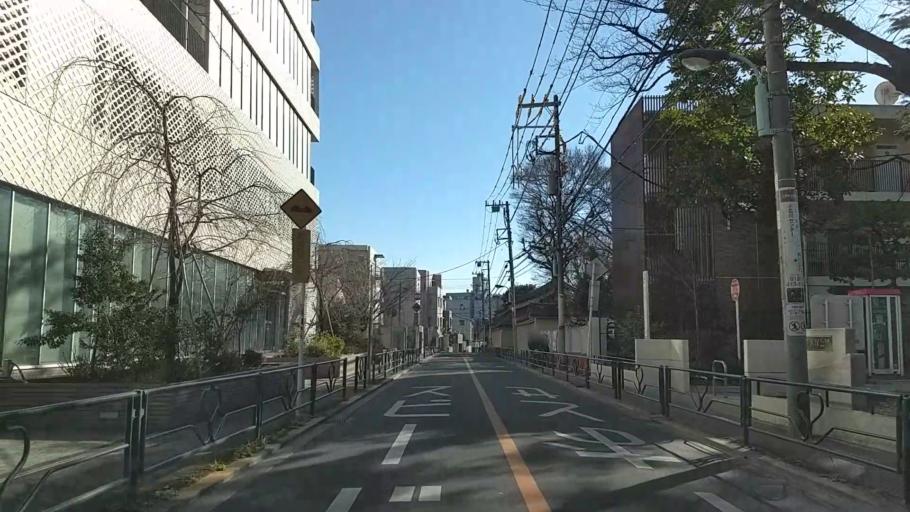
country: JP
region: Tokyo
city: Tokyo
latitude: 35.7174
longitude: 139.7340
